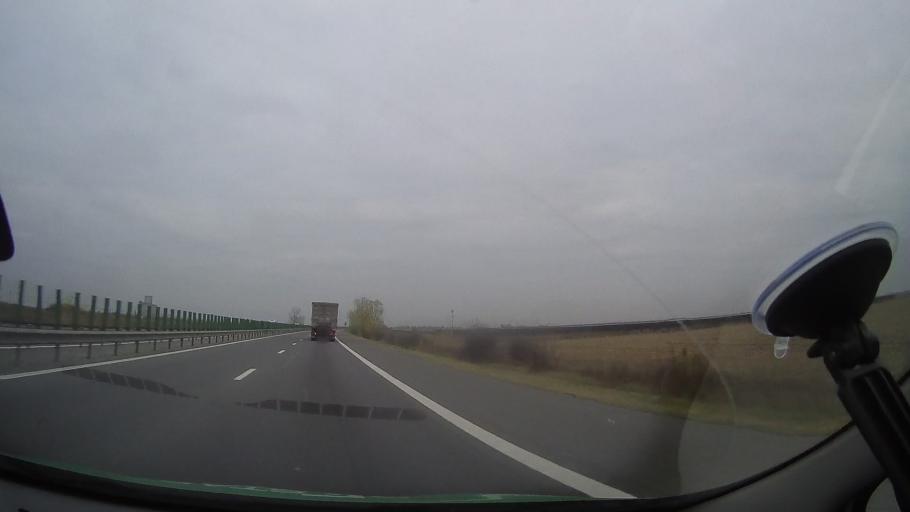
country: RO
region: Calarasi
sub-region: Comuna Sarulesti
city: Sarulesti-Gara
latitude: 44.4474
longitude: 26.6297
